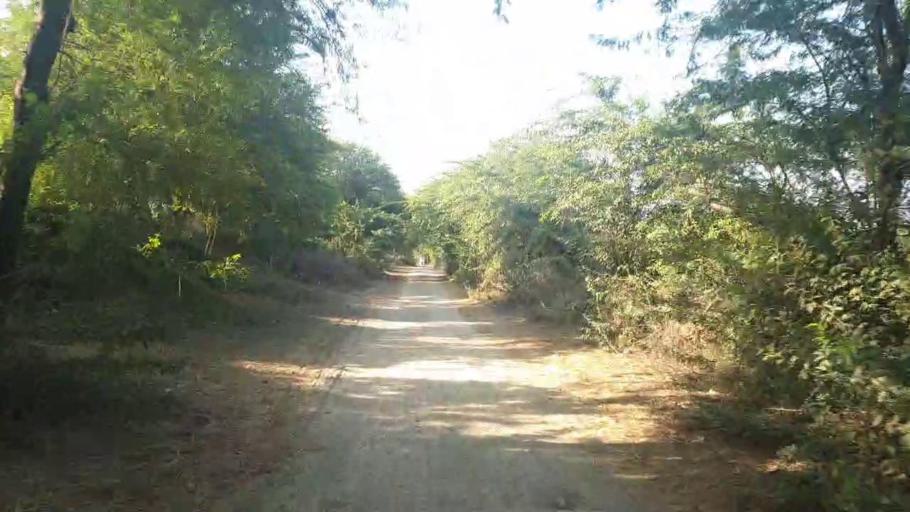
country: PK
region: Sindh
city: Tando Bago
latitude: 24.7450
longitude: 68.9322
